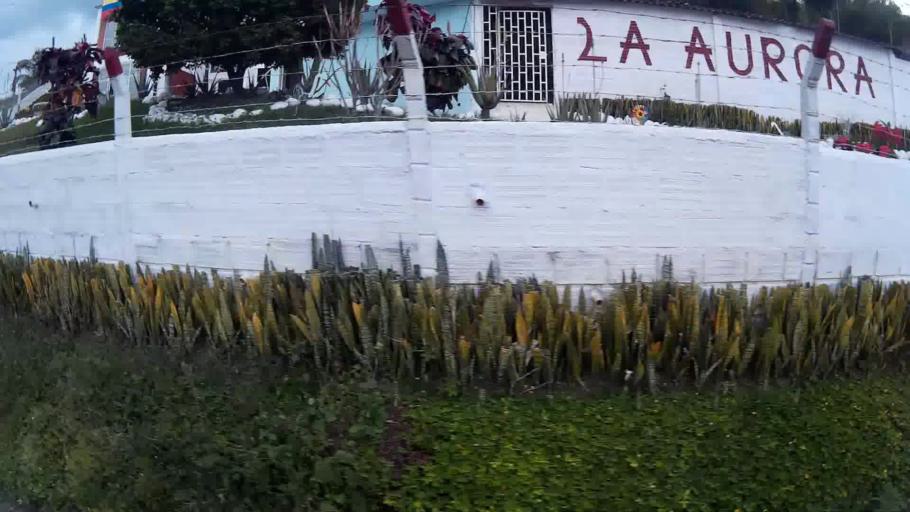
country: CO
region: Risaralda
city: Pereira
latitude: 4.7665
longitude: -75.7191
